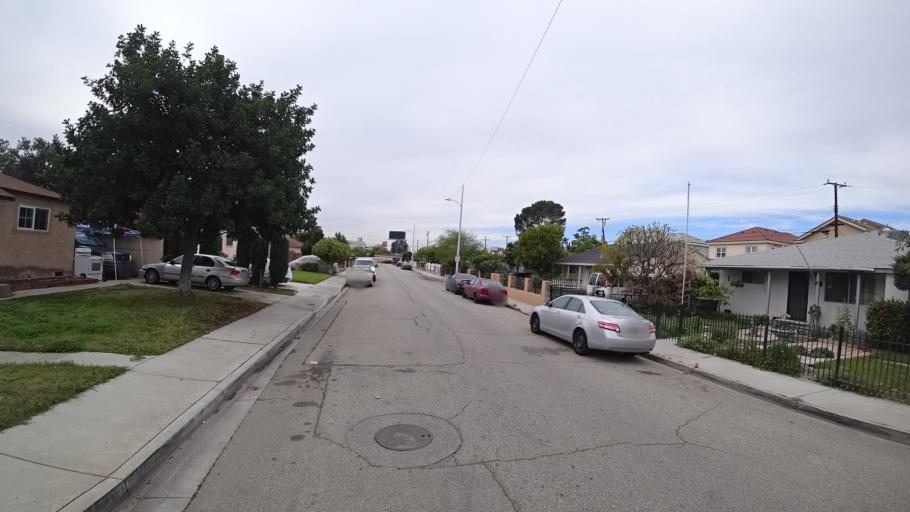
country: US
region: California
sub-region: Los Angeles County
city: West Puente Valley
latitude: 34.0691
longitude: -117.9853
